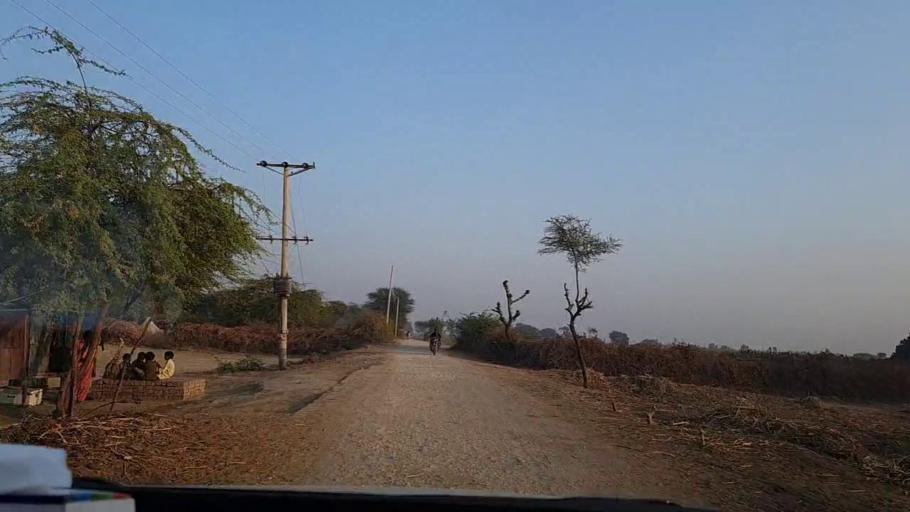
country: PK
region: Sindh
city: Tando Ghulam Ali
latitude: 25.1831
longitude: 68.9213
